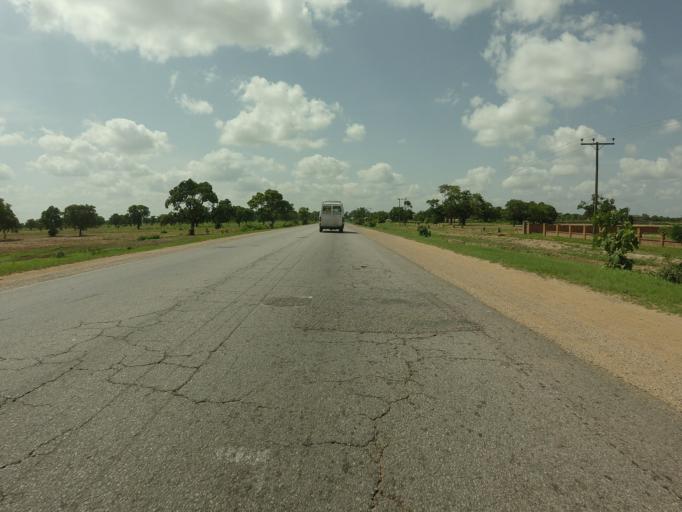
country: GH
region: Northern
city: Savelugu
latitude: 9.5683
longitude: -0.8354
